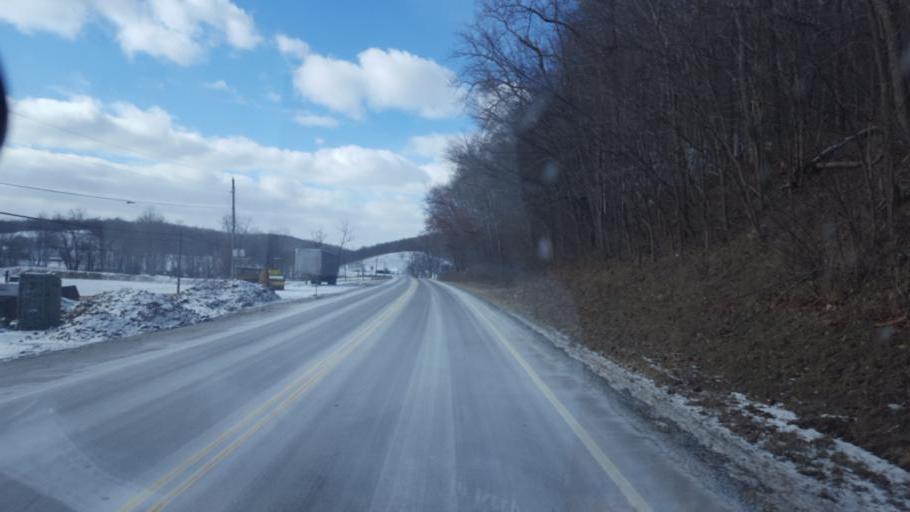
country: US
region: Ohio
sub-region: Knox County
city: Oak Hill
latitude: 40.3425
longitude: -82.0600
